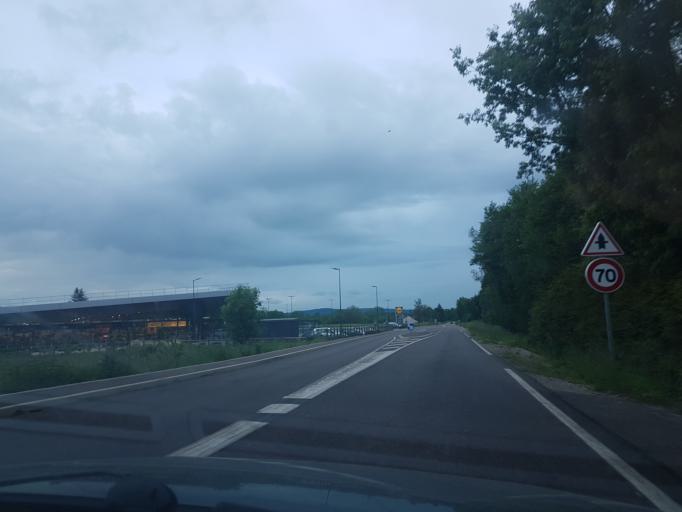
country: FR
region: Franche-Comte
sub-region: Departement de la Haute-Saone
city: Saint-Sauveur
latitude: 47.8165
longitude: 6.3914
